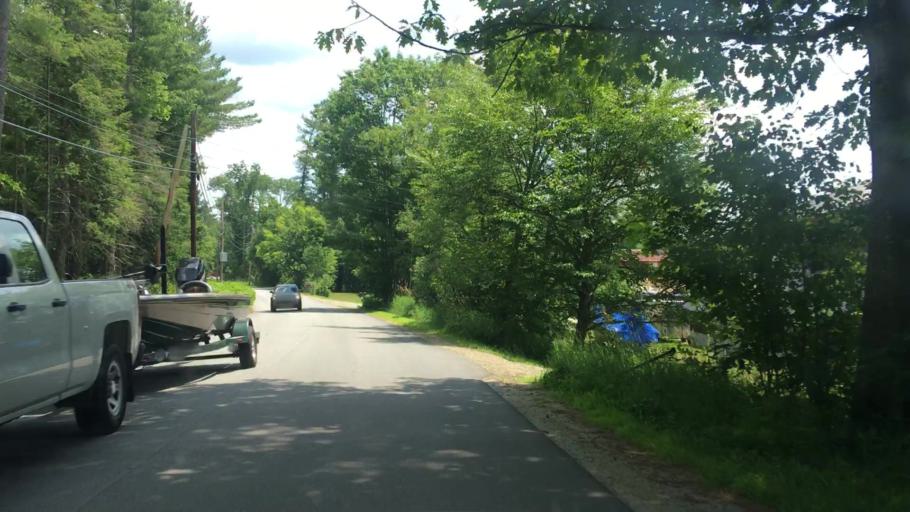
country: US
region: New Hampshire
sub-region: Grafton County
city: Enfield
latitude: 43.6537
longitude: -72.0949
